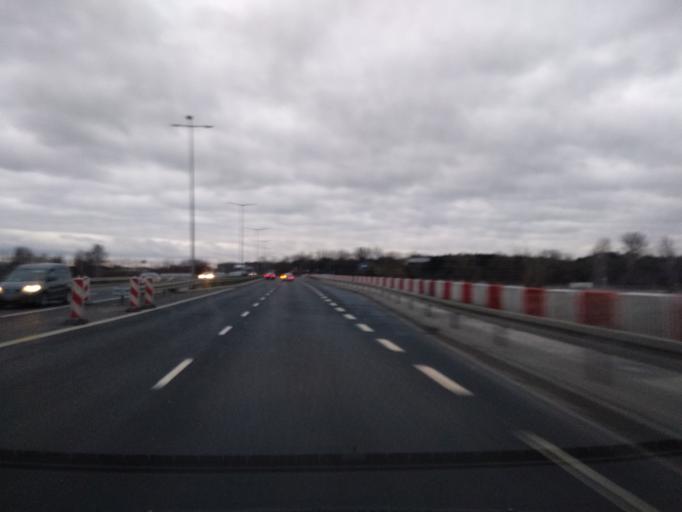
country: PL
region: Greater Poland Voivodeship
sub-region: Konin
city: Konin
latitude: 52.2136
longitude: 18.2286
